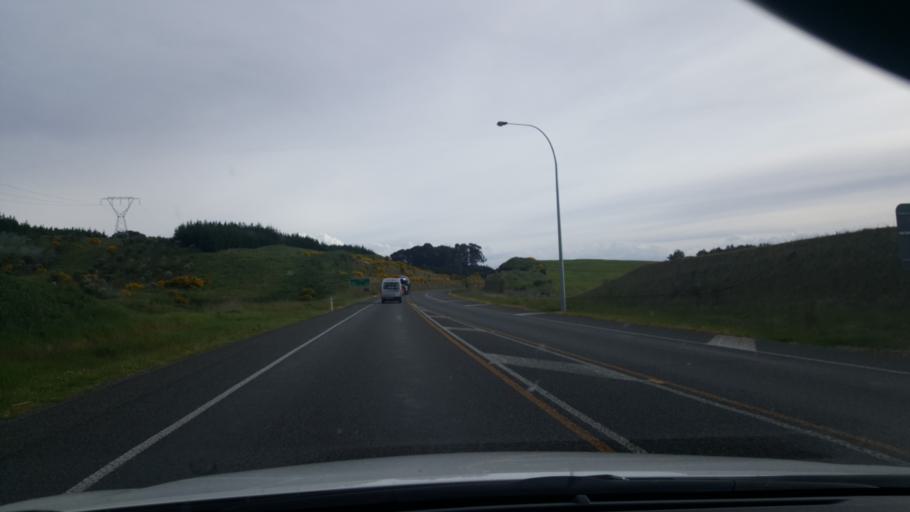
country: NZ
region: Waikato
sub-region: Taupo District
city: Taupo
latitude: -38.7071
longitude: 176.1119
